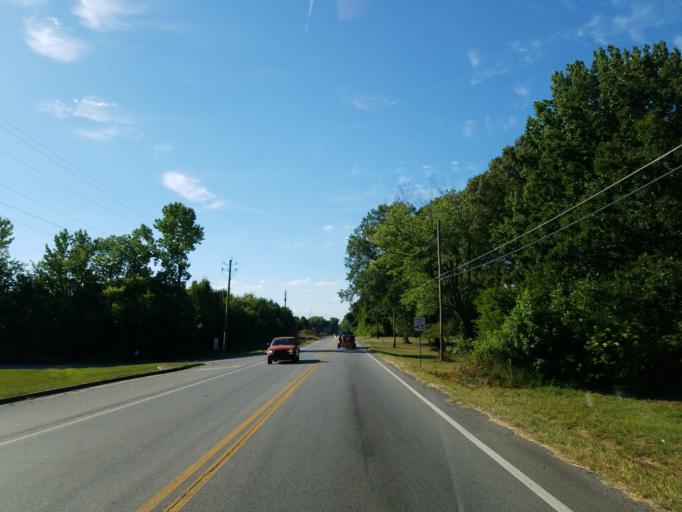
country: US
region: Georgia
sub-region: Gordon County
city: Calhoun
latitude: 34.5609
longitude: -84.9372
